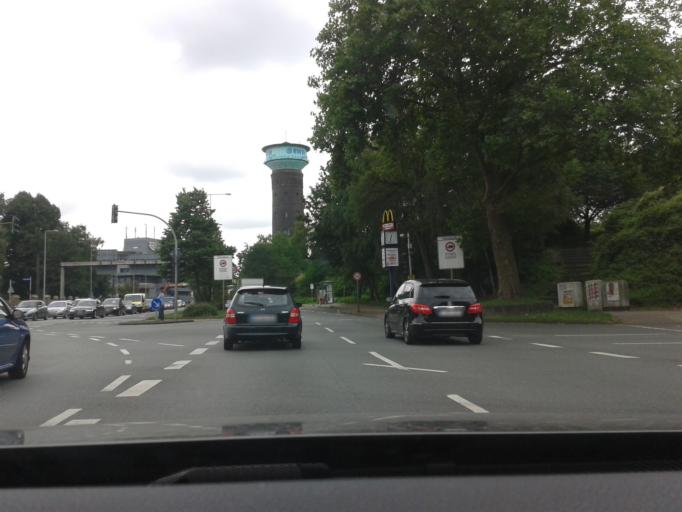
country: DE
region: North Rhine-Westphalia
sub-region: Regierungsbezirk Dusseldorf
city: Oberhausen
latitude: 51.4881
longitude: 6.8628
